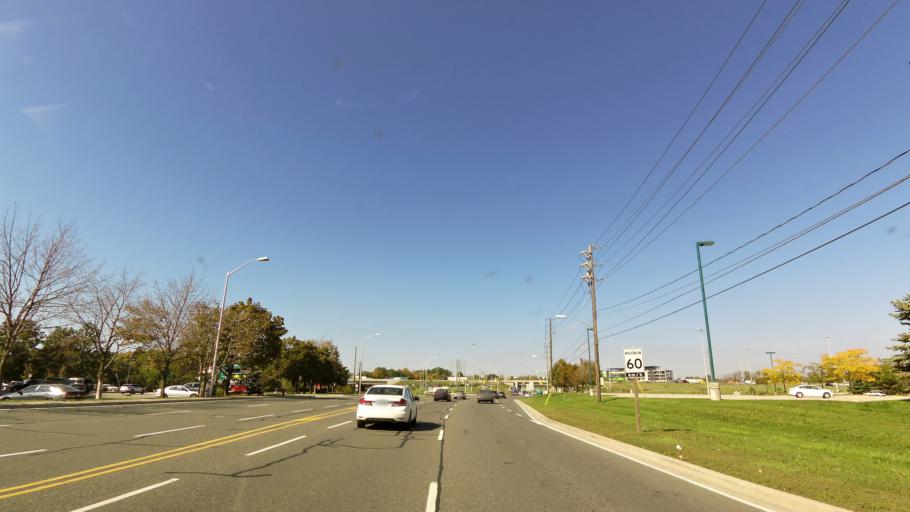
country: CA
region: Ontario
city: Oakville
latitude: 43.4072
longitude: -79.7371
